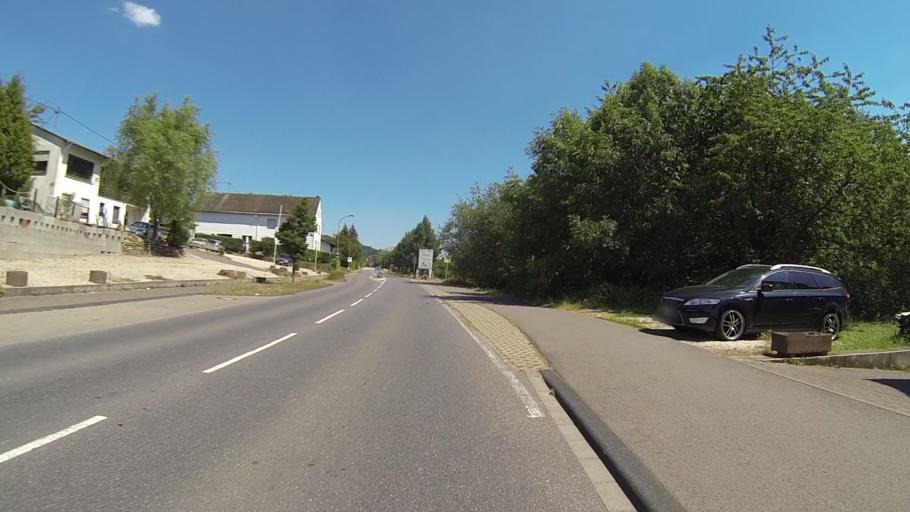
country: LU
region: Grevenmacher
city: Wasserbillig
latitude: 49.7123
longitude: 6.5114
